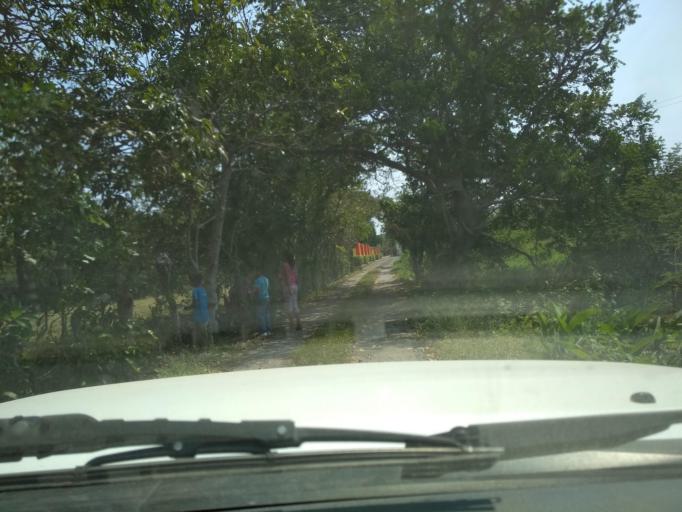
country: MX
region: Veracruz
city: Boca del Rio
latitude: 19.0998
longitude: -96.1245
